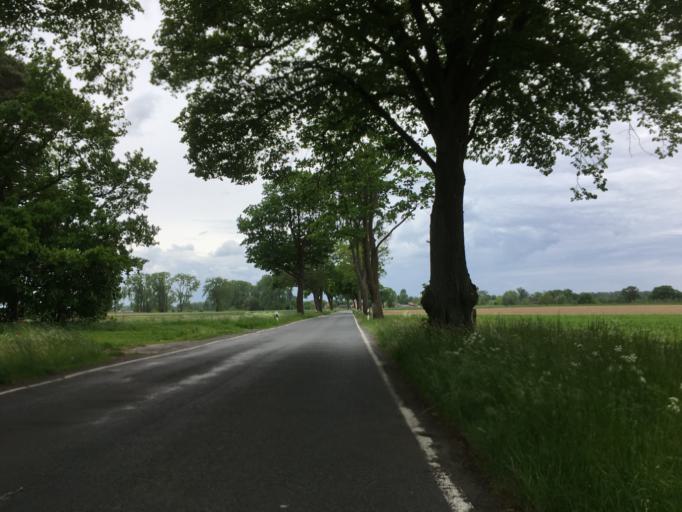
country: DE
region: Brandenburg
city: Werneuchen
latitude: 52.6688
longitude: 13.6975
